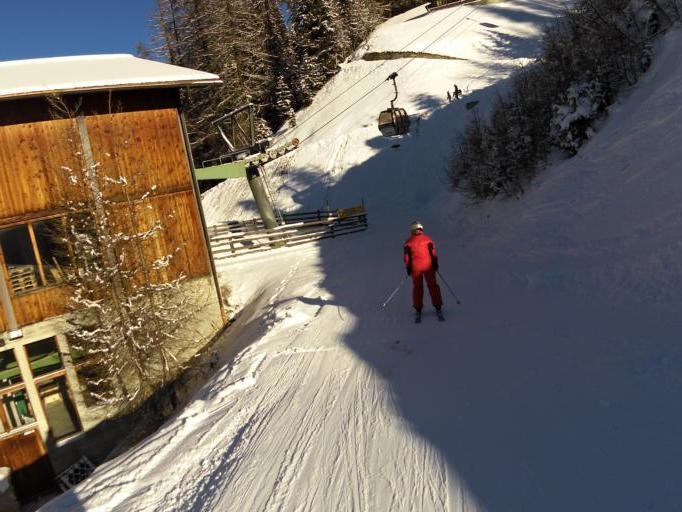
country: CH
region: Grisons
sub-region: Praettigau/Davos District
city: Davos
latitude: 46.7452
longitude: 9.7806
